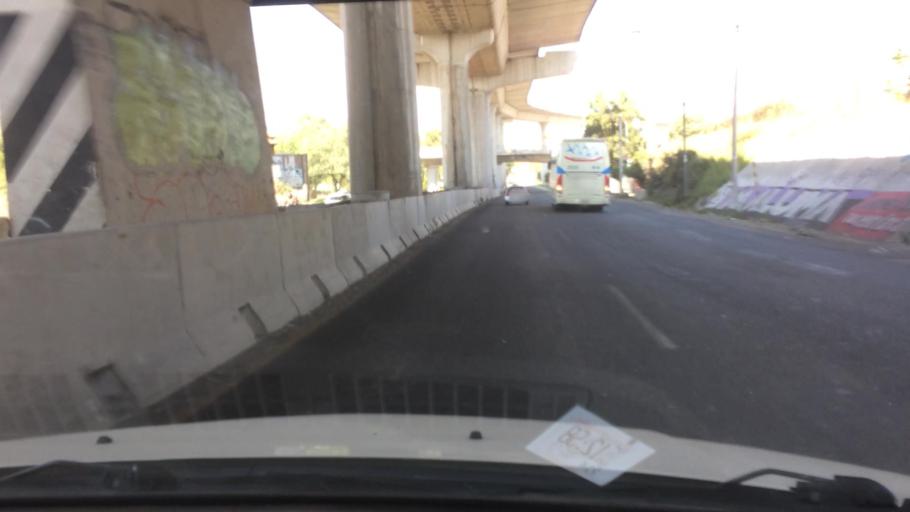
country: MX
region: Mexico City
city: Tlalpan
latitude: 19.2735
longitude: -99.1647
